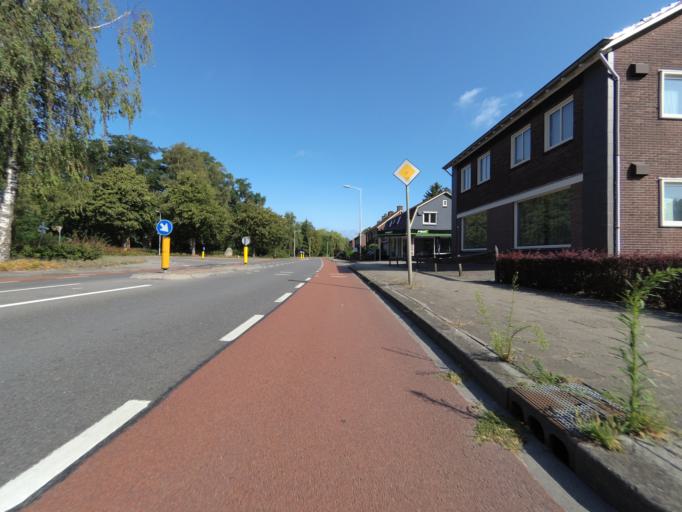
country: NL
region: Overijssel
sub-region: Gemeente Oldenzaal
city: Oldenzaal
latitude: 52.3009
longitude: 6.9312
